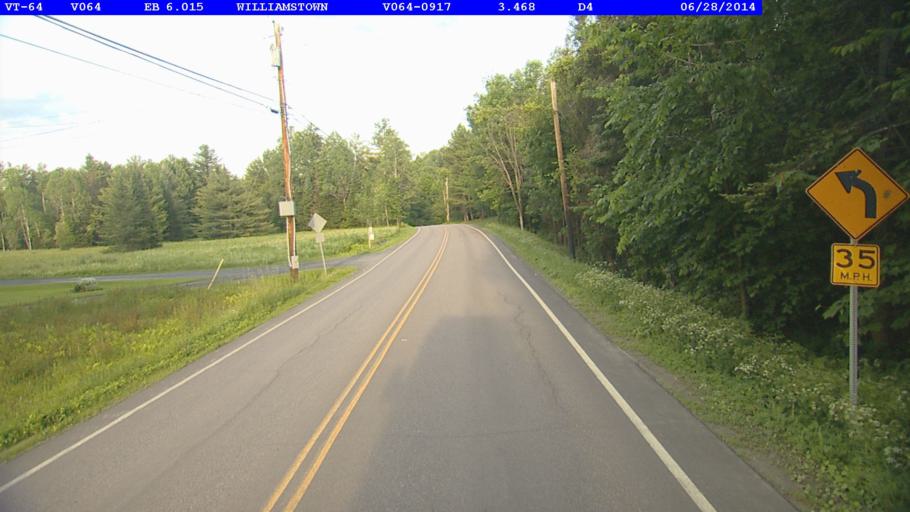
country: US
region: Vermont
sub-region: Orange County
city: Williamstown
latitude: 44.1191
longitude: -72.5547
